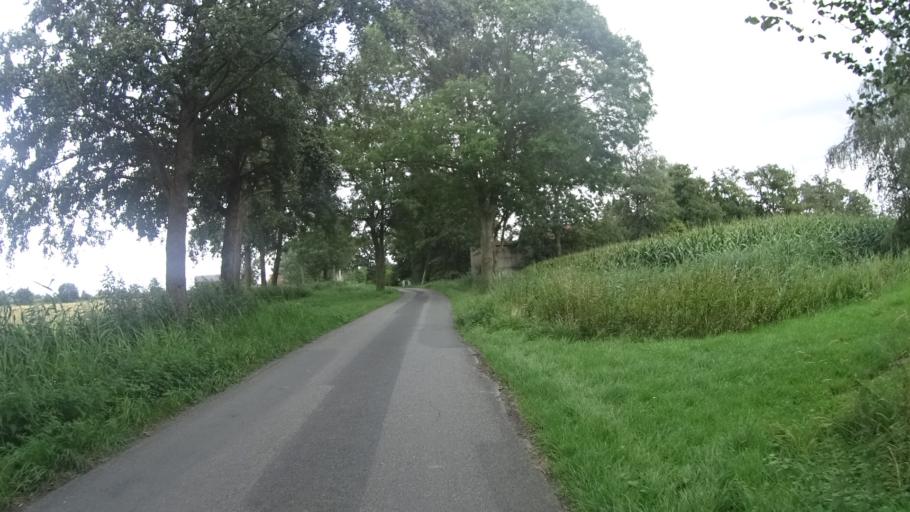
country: DE
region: Lower Saxony
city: Grossenworden
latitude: 53.6981
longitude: 9.2415
